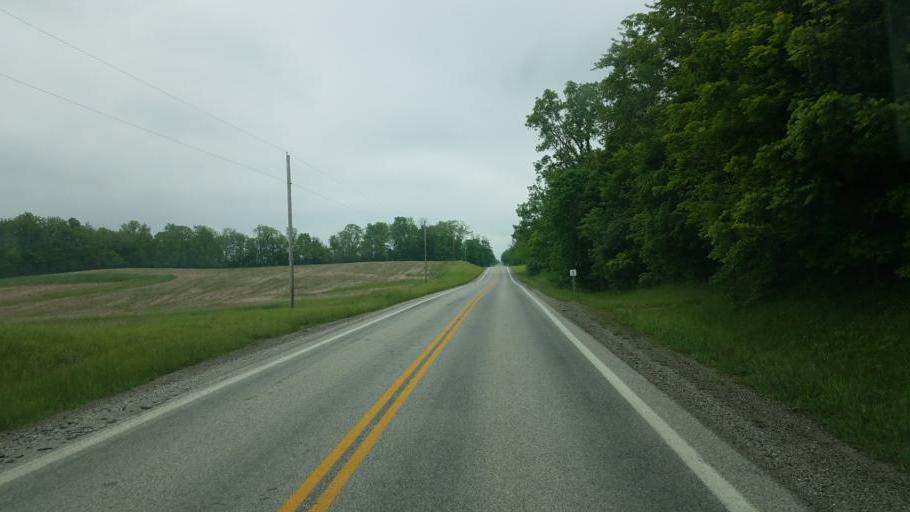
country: US
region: Ohio
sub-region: Knox County
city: Centerburg
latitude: 40.3769
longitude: -82.7315
